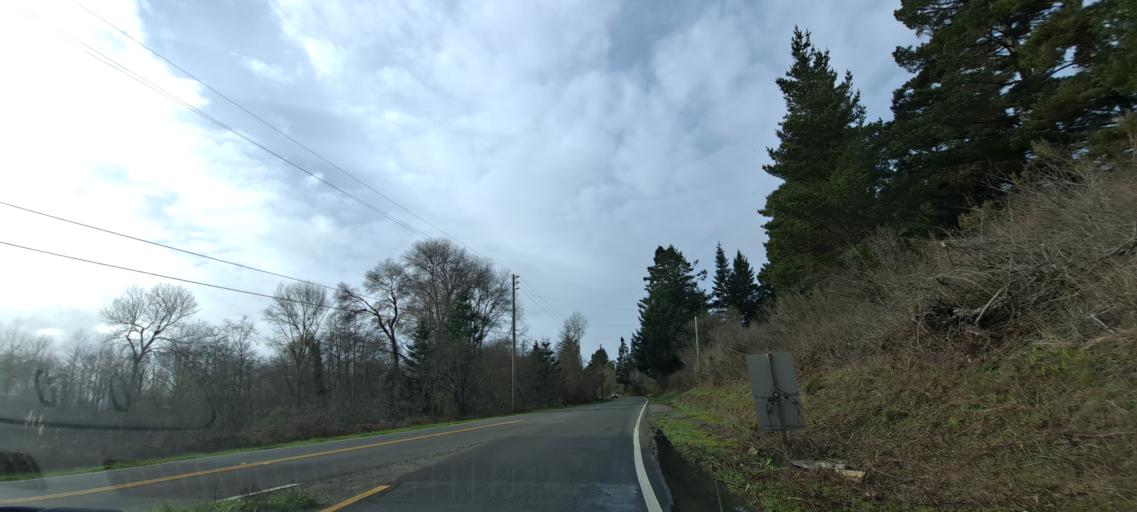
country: US
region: California
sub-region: Humboldt County
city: Fortuna
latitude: 40.6124
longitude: -124.1921
